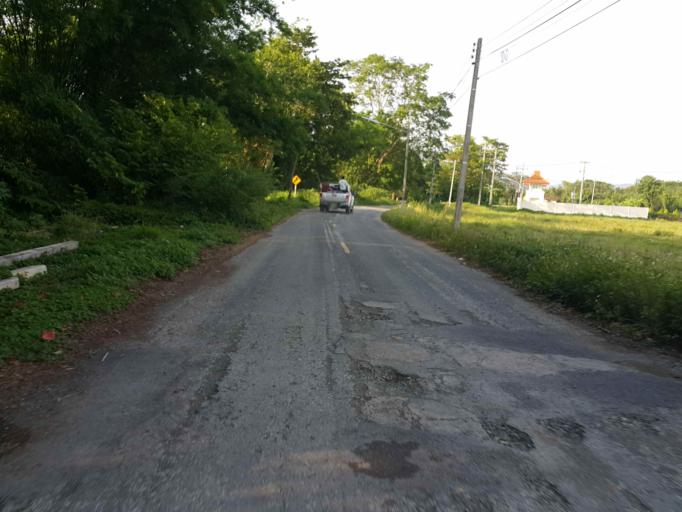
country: TH
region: Chiang Mai
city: San Sai
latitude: 18.8401
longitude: 99.0943
